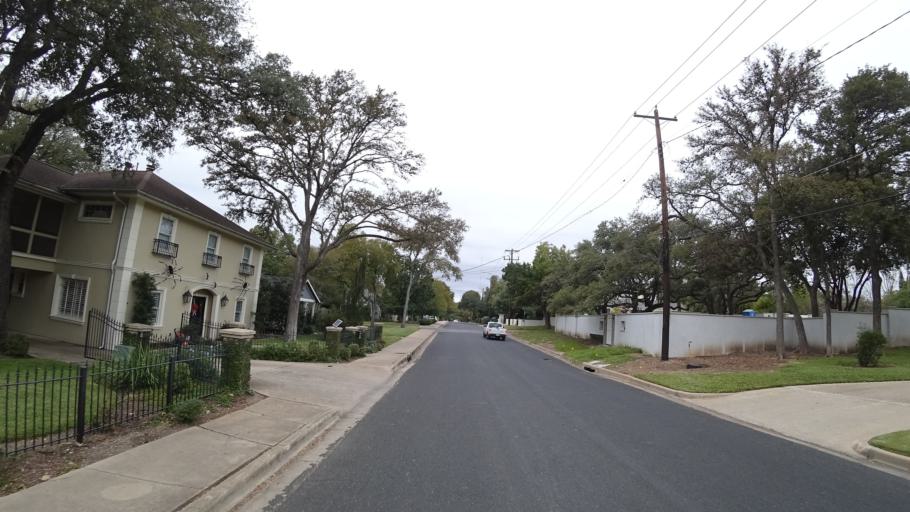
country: US
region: Texas
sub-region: Travis County
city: Rollingwood
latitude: 30.2987
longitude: -97.7716
